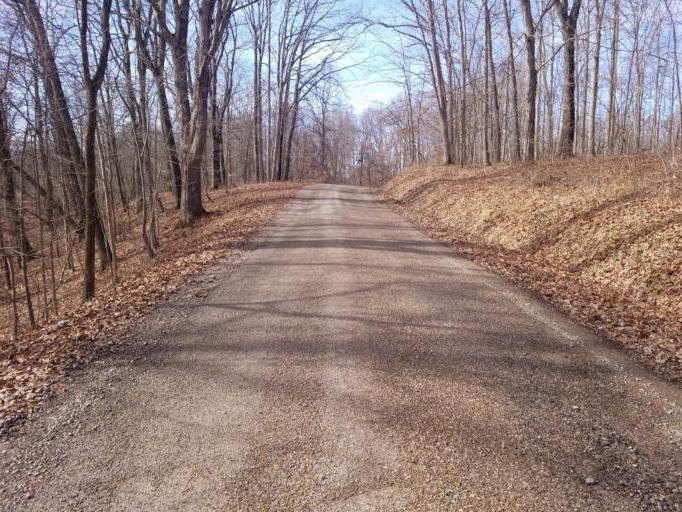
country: US
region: Ohio
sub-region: Athens County
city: Glouster
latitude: 39.5349
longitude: -82.0883
